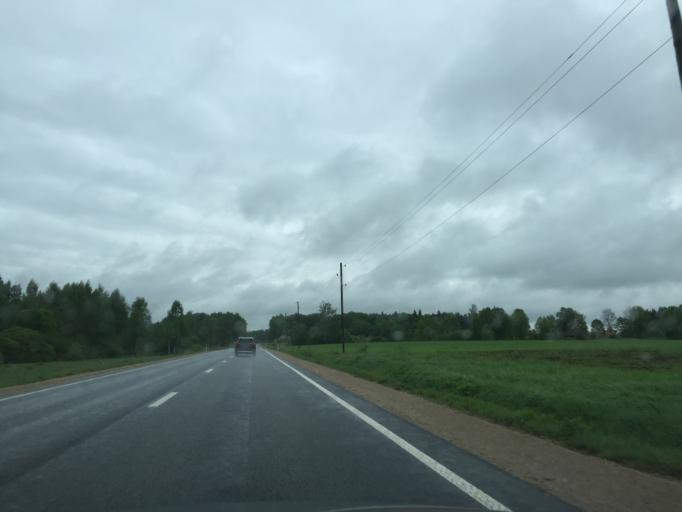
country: LV
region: Ogre
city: Jumprava
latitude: 56.6746
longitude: 24.8976
